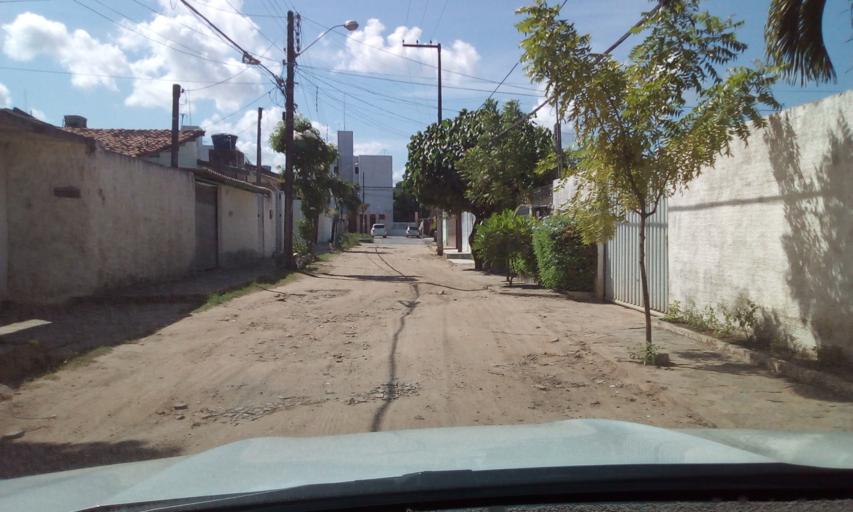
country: BR
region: Paraiba
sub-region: Joao Pessoa
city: Joao Pessoa
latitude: -7.1528
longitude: -34.8475
